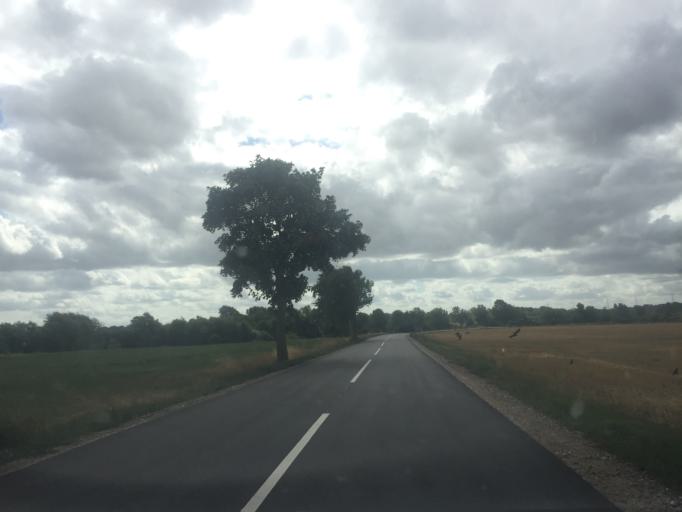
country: DK
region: Capital Region
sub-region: Egedal Kommune
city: Vekso
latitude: 55.7008
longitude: 12.2302
